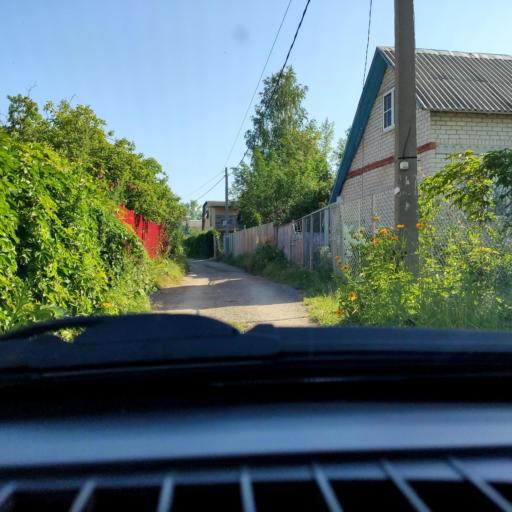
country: RU
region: Samara
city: Zhigulevsk
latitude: 53.4540
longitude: 49.5443
